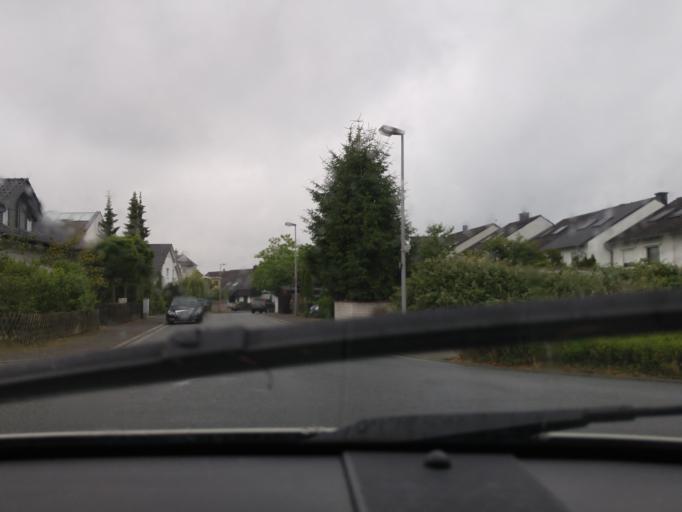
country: DE
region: Hesse
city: Dreieich
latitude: 50.0210
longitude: 8.7025
